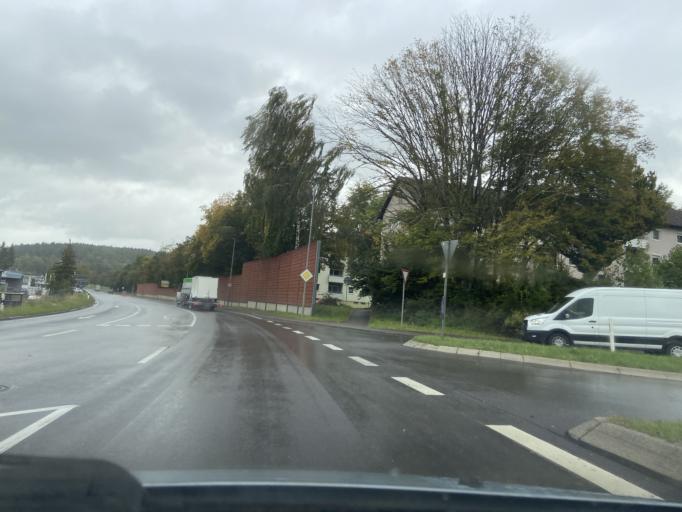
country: DE
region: Baden-Wuerttemberg
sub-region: Tuebingen Region
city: Messkirch
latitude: 47.9962
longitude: 9.1212
